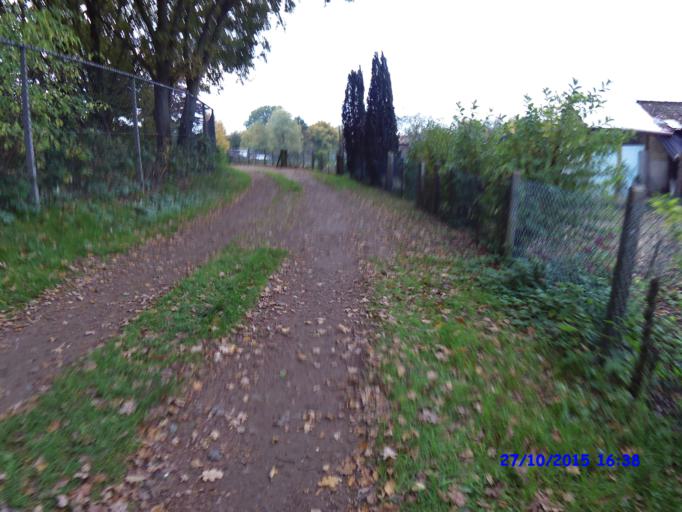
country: BE
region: Flanders
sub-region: Provincie Antwerpen
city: Brasschaat
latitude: 51.2662
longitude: 4.4561
